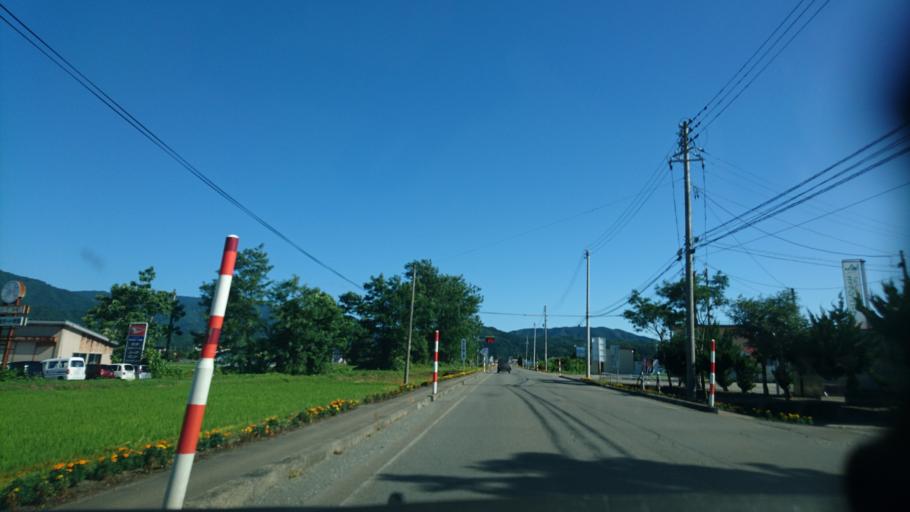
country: JP
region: Akita
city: Kakunodatemachi
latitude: 39.6559
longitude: 140.5707
